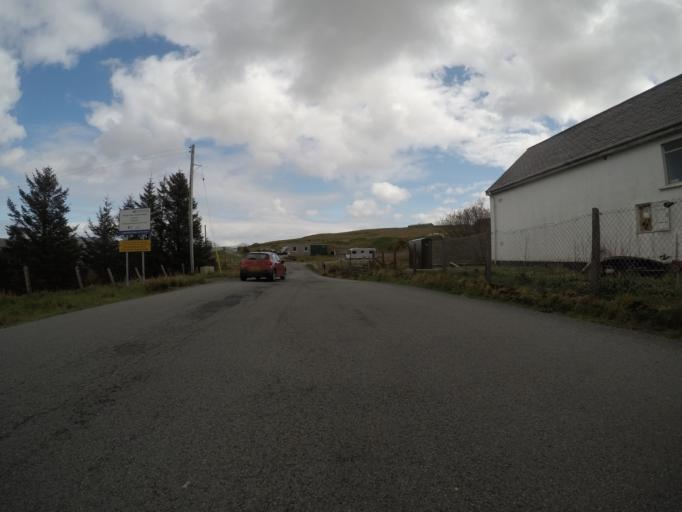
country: GB
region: Scotland
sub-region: Highland
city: Isle of Skye
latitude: 57.2950
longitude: -6.3354
